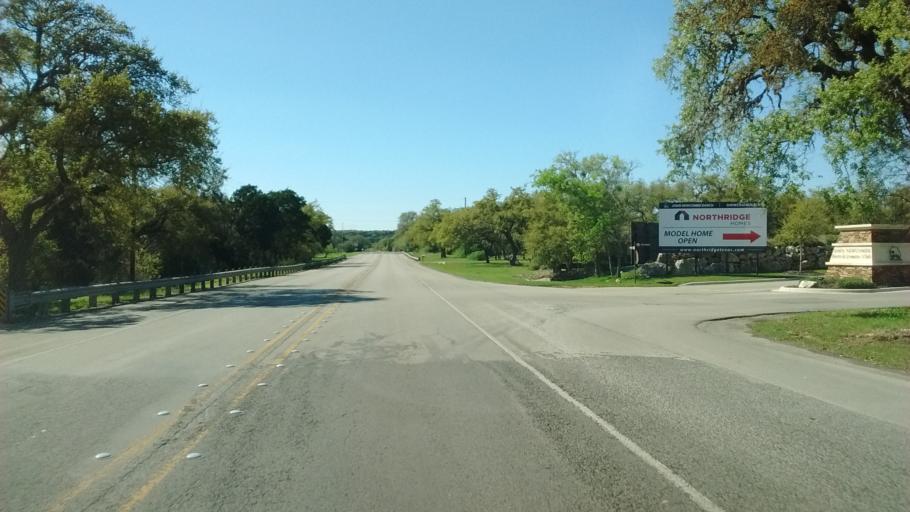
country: US
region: Texas
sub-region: Comal County
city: New Braunfels
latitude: 29.7128
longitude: -98.2056
